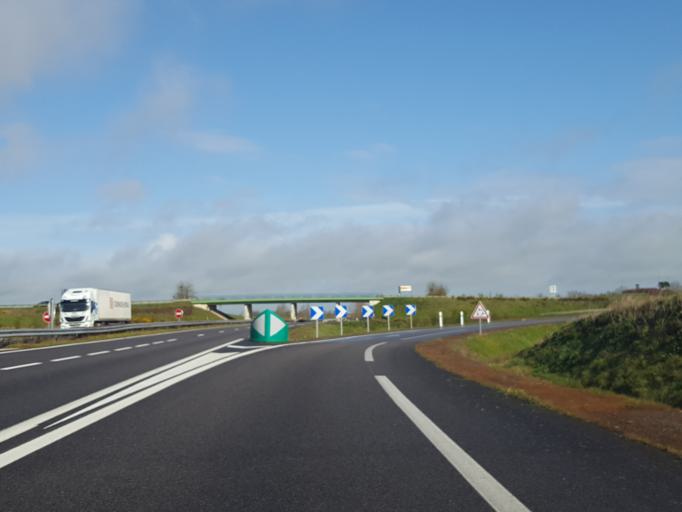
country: FR
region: Pays de la Loire
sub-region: Departement de la Vendee
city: Belleville-sur-Vie
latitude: 46.7959
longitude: -1.4290
